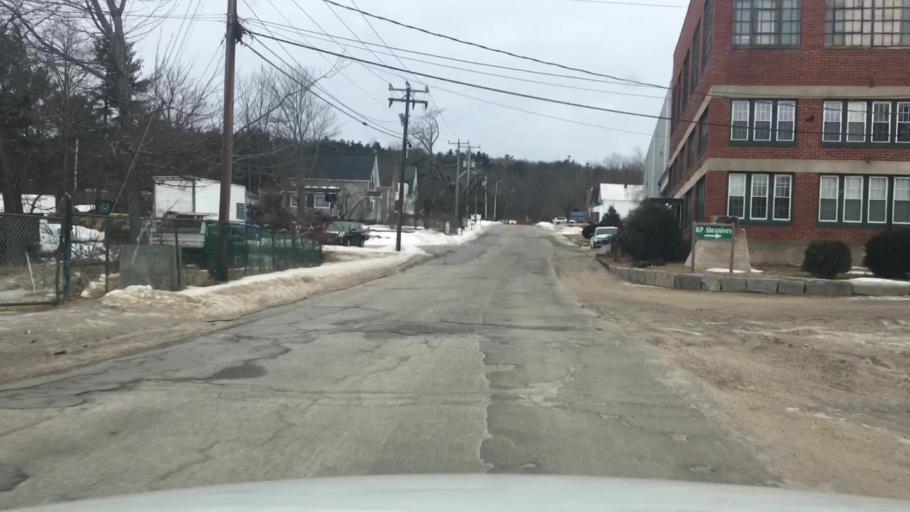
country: US
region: New Hampshire
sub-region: Strafford County
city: Rochester
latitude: 43.3735
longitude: -70.9822
